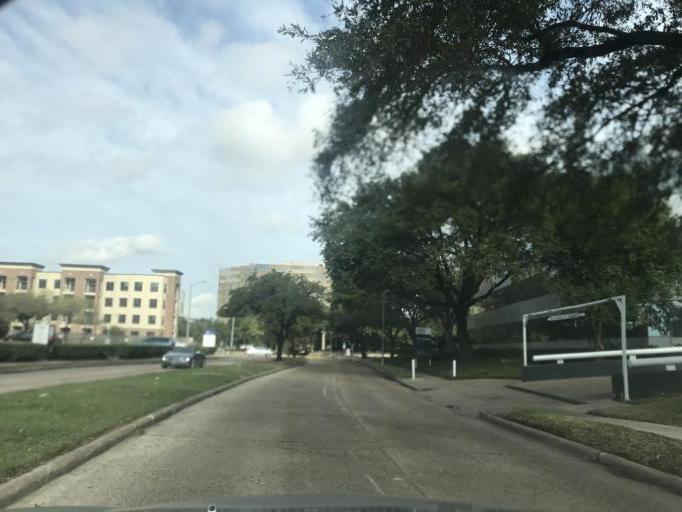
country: US
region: Texas
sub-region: Harris County
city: Hunters Creek Village
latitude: 29.7391
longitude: -95.4844
